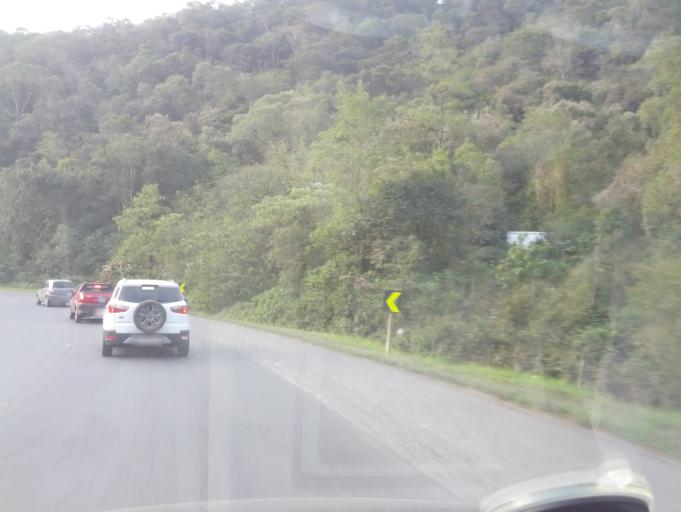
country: BR
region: Santa Catarina
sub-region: Otacilio Costa
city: Otacilio Costa
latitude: -27.2971
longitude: -50.0750
